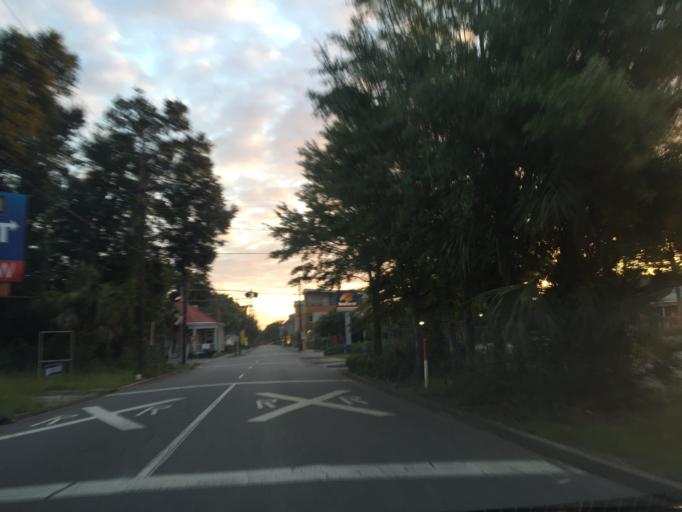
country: US
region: Georgia
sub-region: Chatham County
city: Savannah
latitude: 32.0527
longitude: -81.1005
